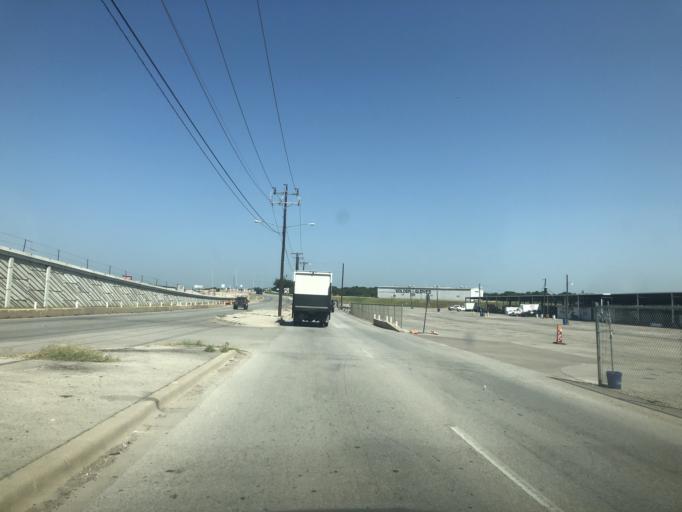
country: US
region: Texas
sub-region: Tarrant County
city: Fort Worth
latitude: 32.7625
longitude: -97.3474
